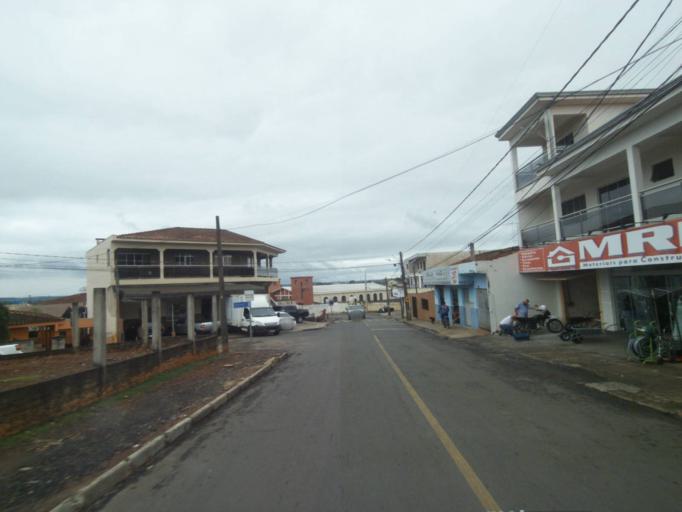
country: BR
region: Parana
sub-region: Telemaco Borba
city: Telemaco Borba
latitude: -24.3267
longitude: -50.6424
